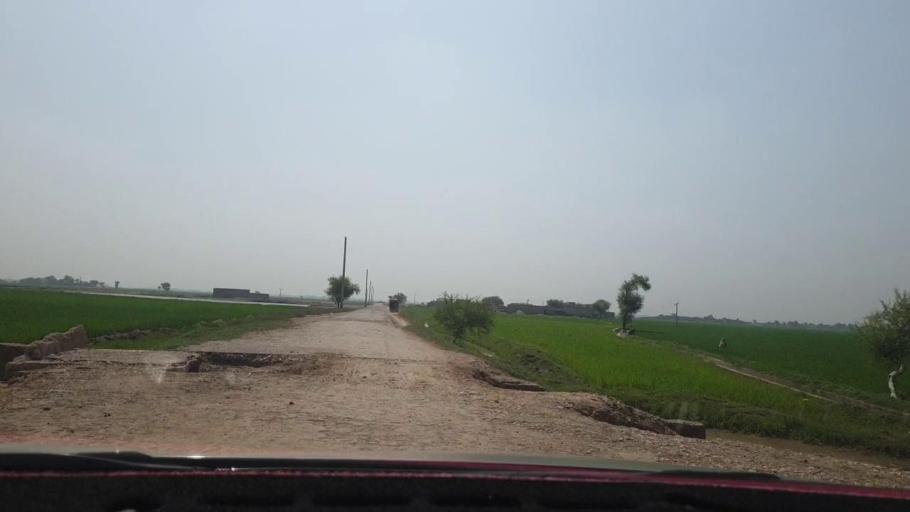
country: PK
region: Sindh
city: Warah
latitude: 27.4064
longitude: 67.8452
